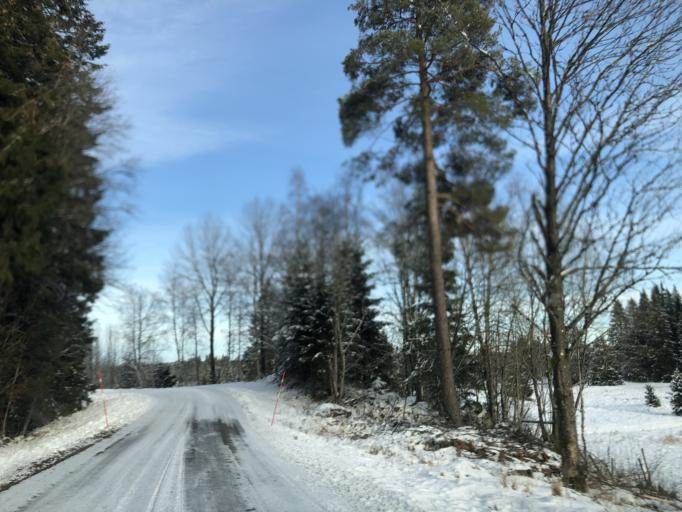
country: SE
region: Vaestra Goetaland
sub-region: Ulricehamns Kommun
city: Ulricehamn
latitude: 57.7657
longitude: 13.5199
